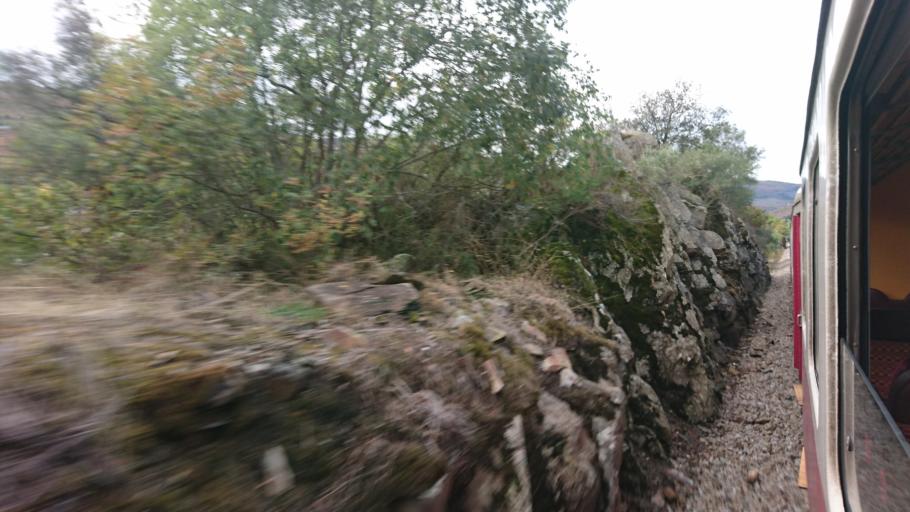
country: PT
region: Viseu
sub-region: Tabuaco
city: Tabuaco
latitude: 41.1728
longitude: -7.5607
